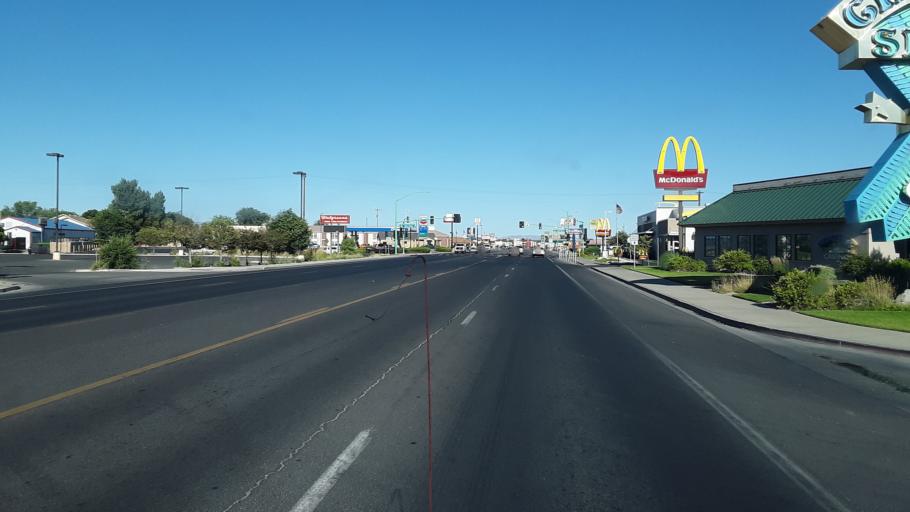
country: US
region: Nevada
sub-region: Churchill County
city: Fallon
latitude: 39.4766
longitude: -118.8019
